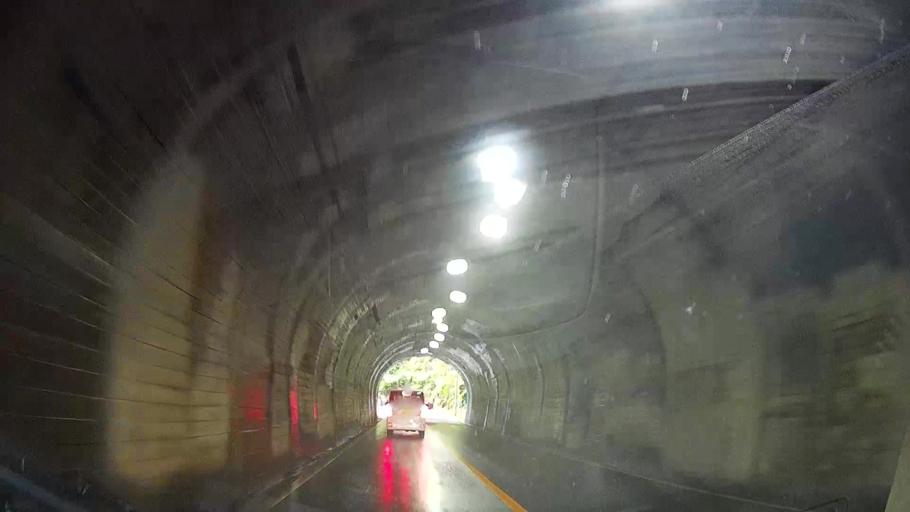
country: JP
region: Oita
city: Hita
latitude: 33.1922
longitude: 130.9947
